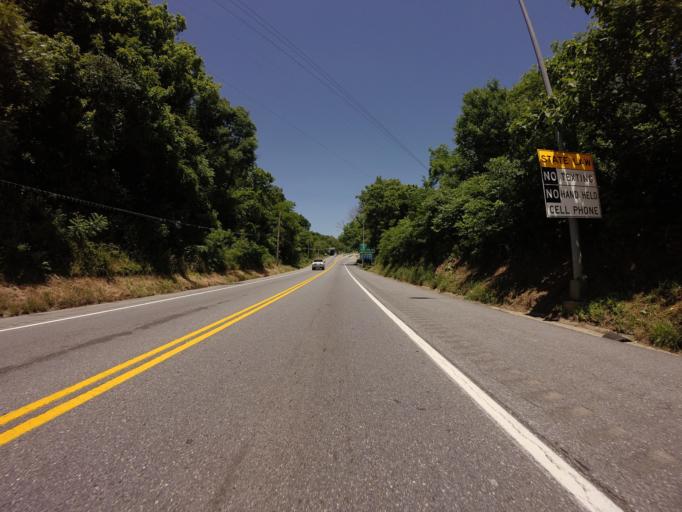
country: US
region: West Virginia
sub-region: Jefferson County
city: Bolivar
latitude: 39.3272
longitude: -77.7055
